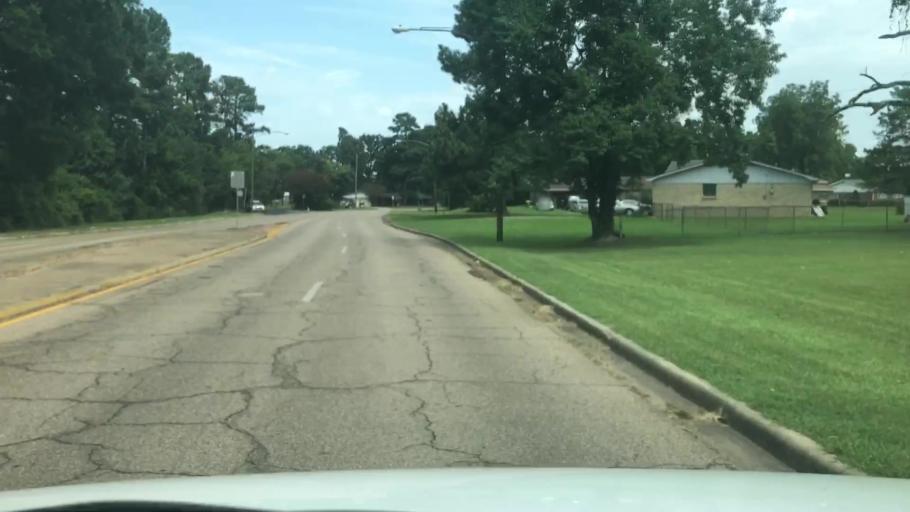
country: US
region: Texas
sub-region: Bowie County
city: Wake Village
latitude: 33.4017
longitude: -94.0802
